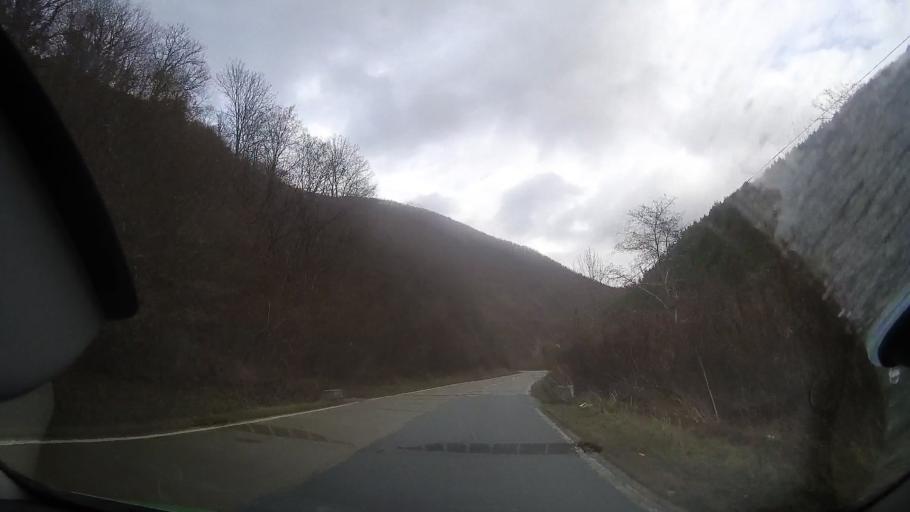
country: RO
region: Alba
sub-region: Comuna Rimetea
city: Rimetea
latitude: 46.5038
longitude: 23.5800
